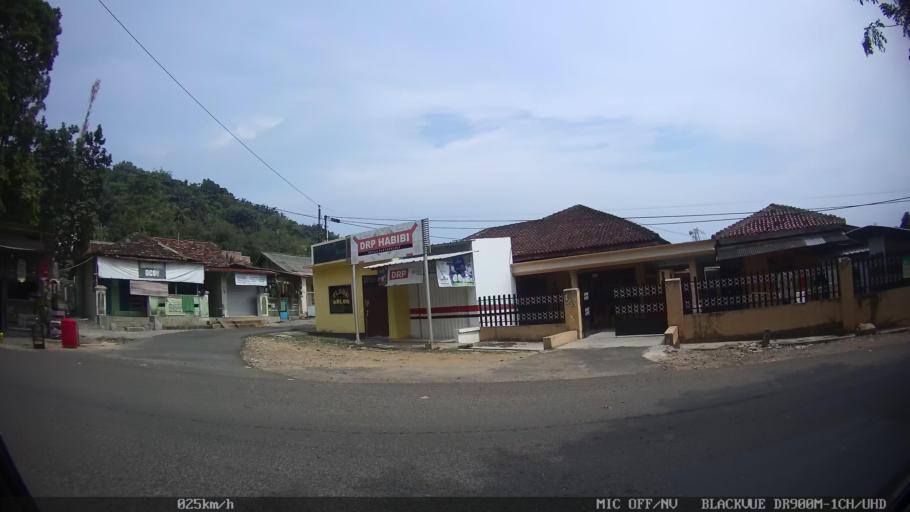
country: ID
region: Lampung
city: Bandarlampung
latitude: -5.4307
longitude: 105.2778
